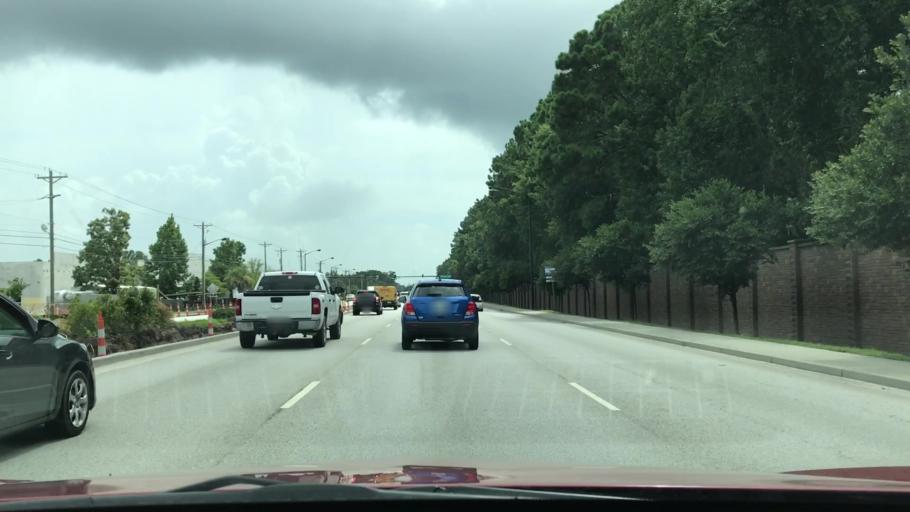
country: US
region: South Carolina
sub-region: Charleston County
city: Isle of Palms
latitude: 32.8433
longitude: -79.8155
